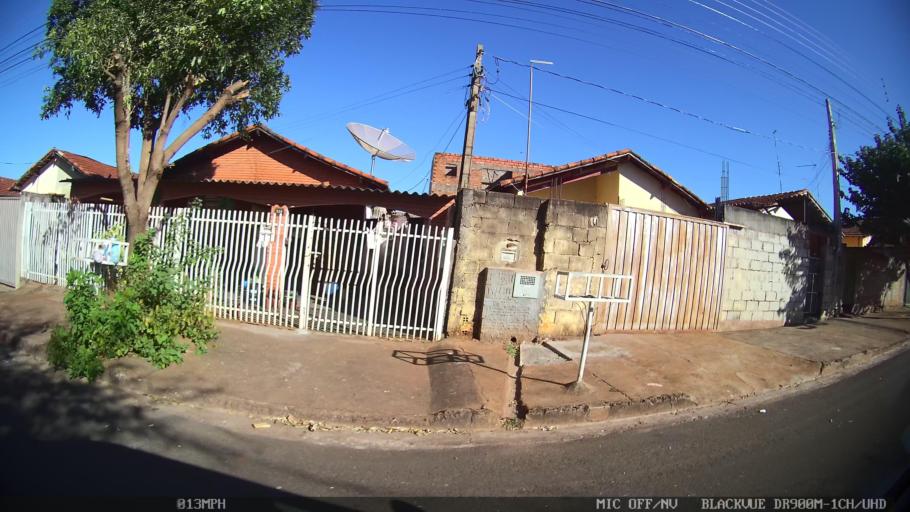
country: BR
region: Sao Paulo
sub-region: Olimpia
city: Olimpia
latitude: -20.7424
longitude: -48.8893
